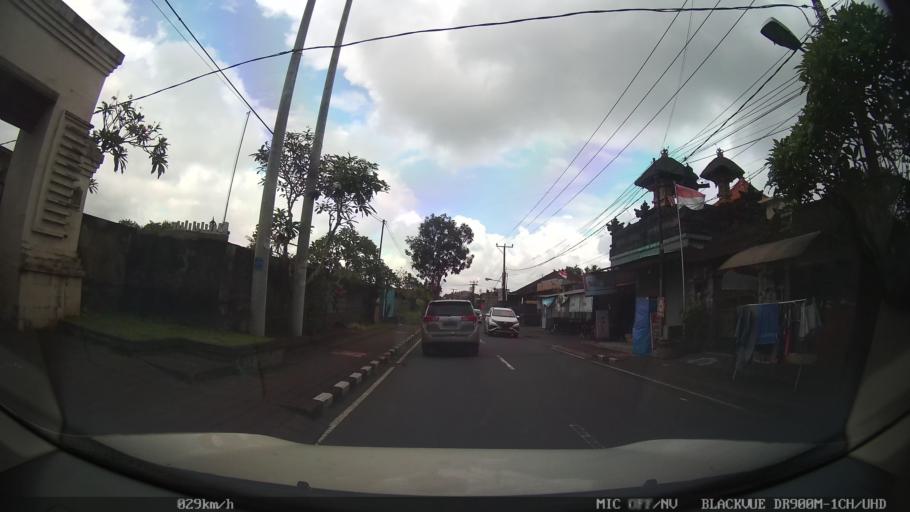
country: ID
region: Bali
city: Banjar Cemenggon
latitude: -8.5306
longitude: 115.2008
